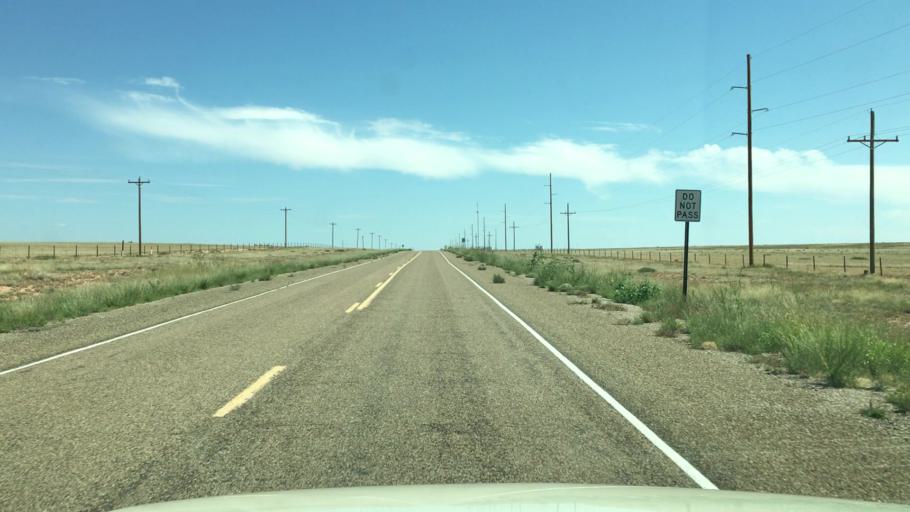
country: US
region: New Mexico
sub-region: Chaves County
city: Roswell
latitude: 33.9507
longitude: -104.5882
